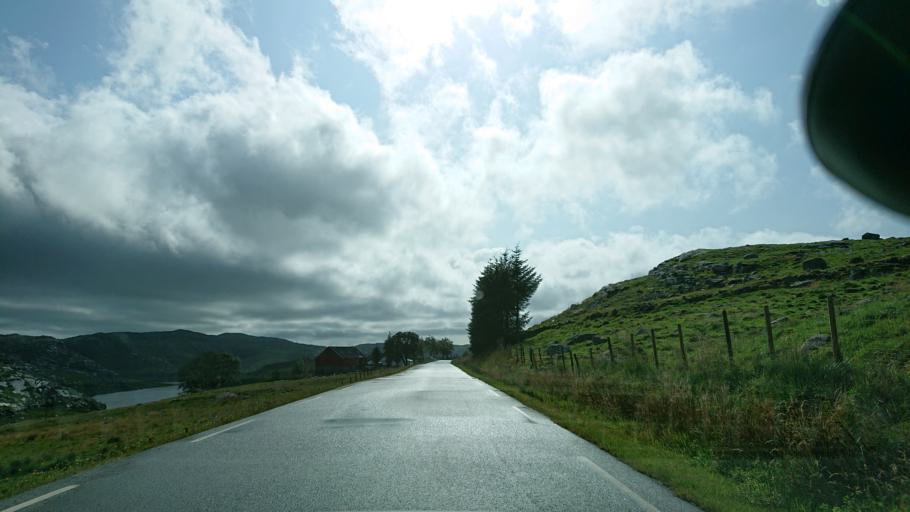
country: NO
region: Rogaland
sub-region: Gjesdal
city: Algard
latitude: 58.6876
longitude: 5.8734
